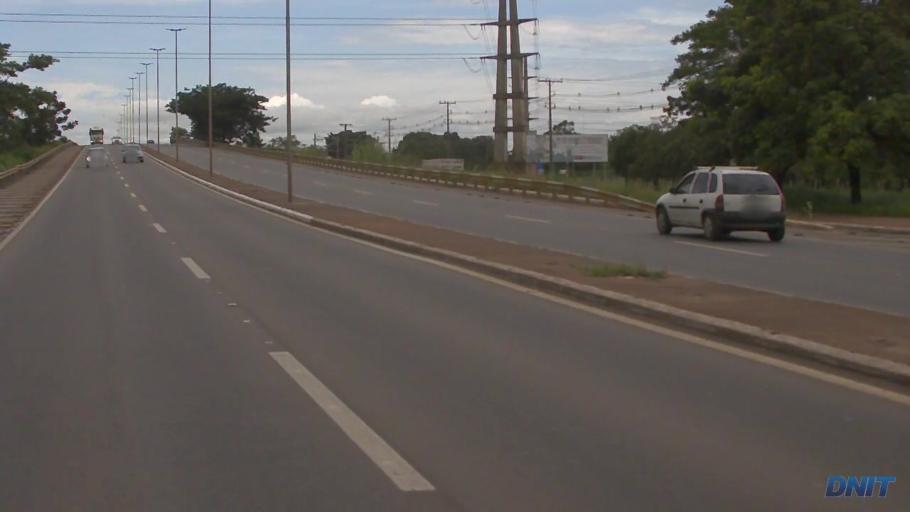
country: BR
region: Mato Grosso
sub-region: Cuiaba
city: Cuiaba
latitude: -15.6483
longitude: -56.0035
